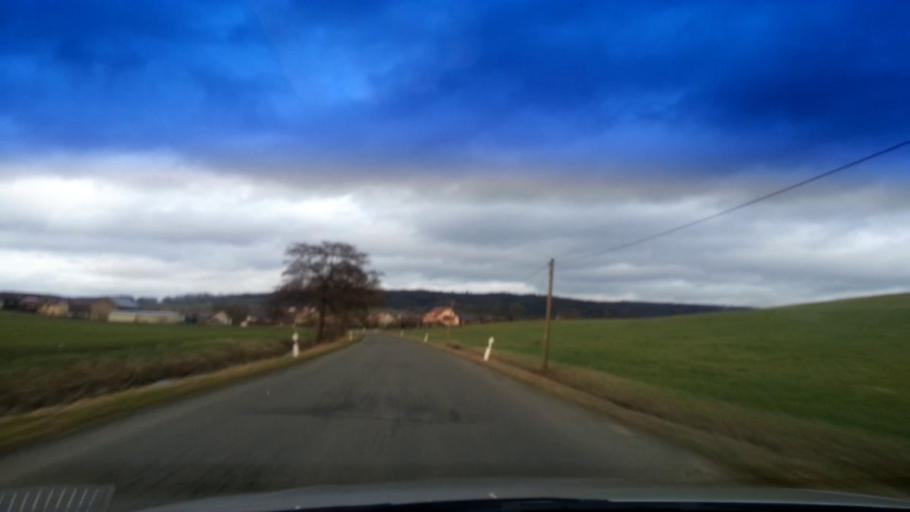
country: DE
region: Bavaria
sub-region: Upper Franconia
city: Schesslitz
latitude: 49.9994
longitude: 11.0148
